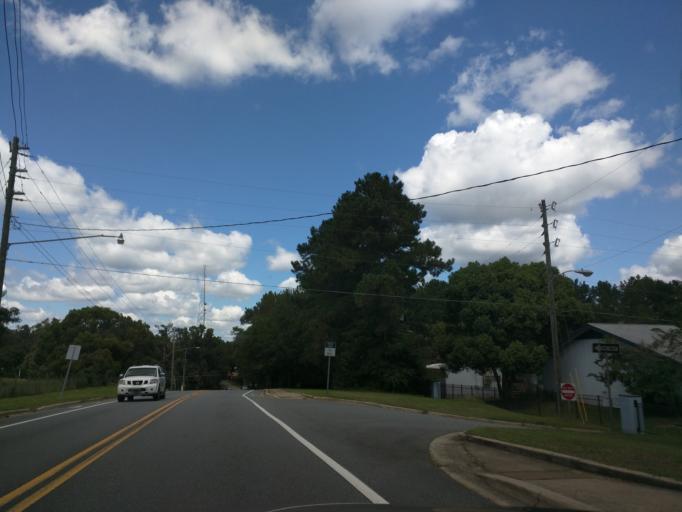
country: US
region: Florida
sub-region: Leon County
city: Tallahassee
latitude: 30.4382
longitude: -84.2188
